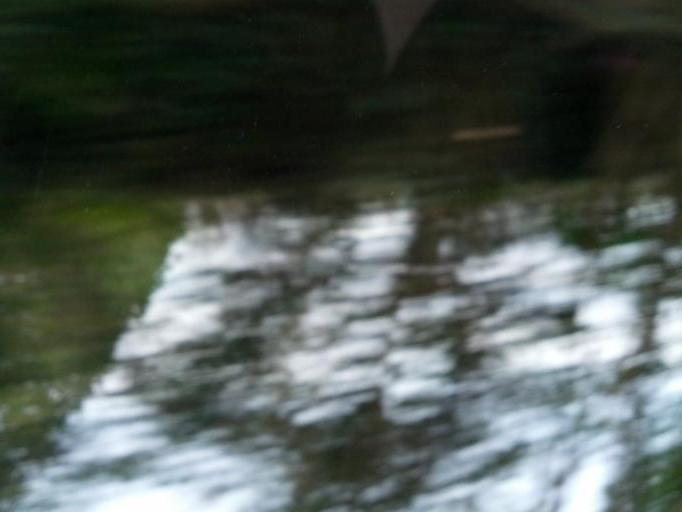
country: IE
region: Connaught
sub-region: County Galway
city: Oranmore
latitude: 53.2356
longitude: -8.8418
